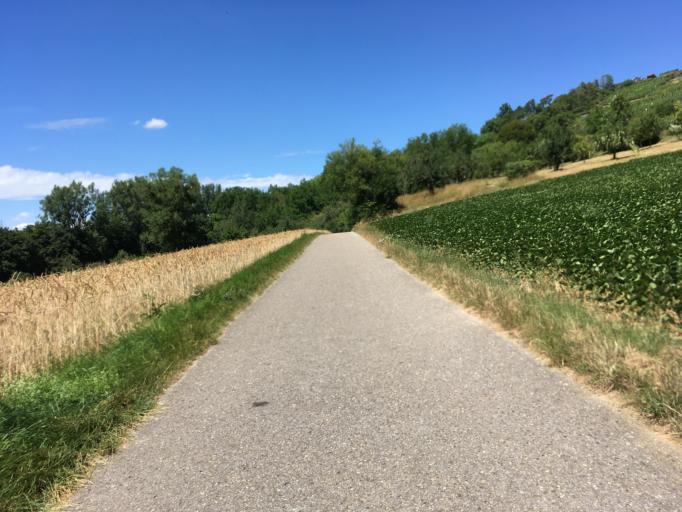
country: DE
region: Baden-Wuerttemberg
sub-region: Karlsruhe Region
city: Illingen
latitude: 48.9371
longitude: 8.9044
